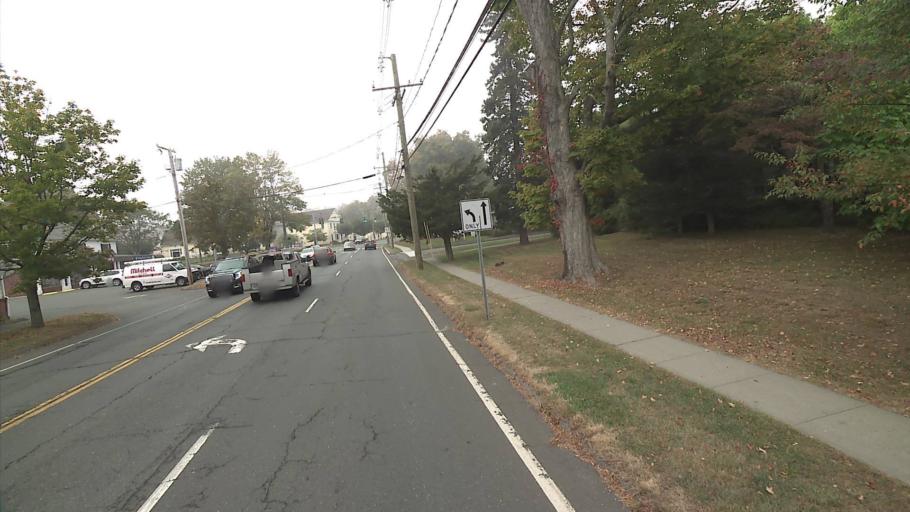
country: US
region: Connecticut
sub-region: Fairfield County
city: Newtown
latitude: 41.4144
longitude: -73.3026
